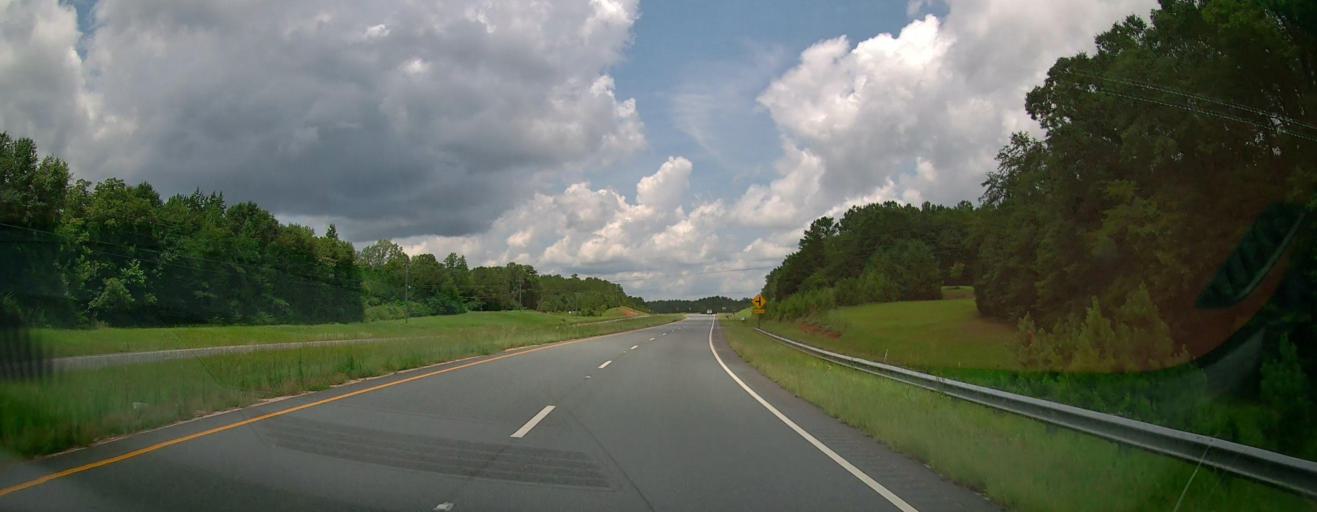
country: US
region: Georgia
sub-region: Upson County
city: Thomaston
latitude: 32.8284
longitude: -84.3075
